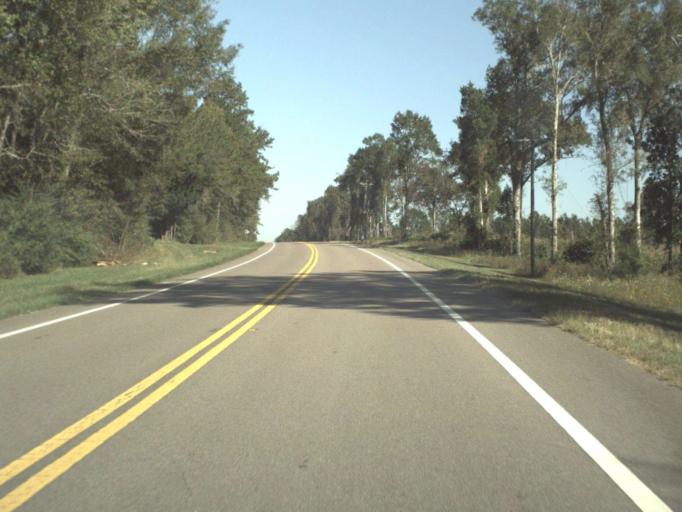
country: US
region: Florida
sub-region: Walton County
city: DeFuniak Springs
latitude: 30.6389
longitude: -85.9366
